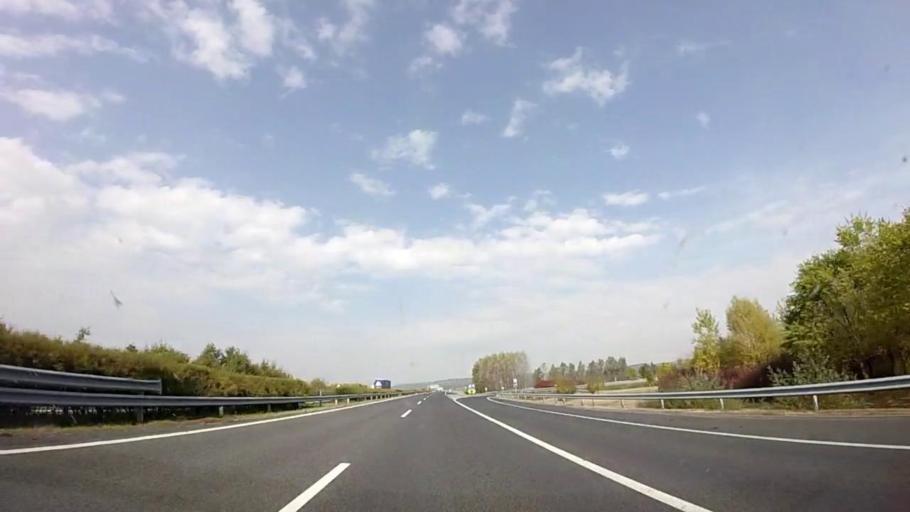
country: HU
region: Zala
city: Letenye
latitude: 46.4230
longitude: 16.7109
